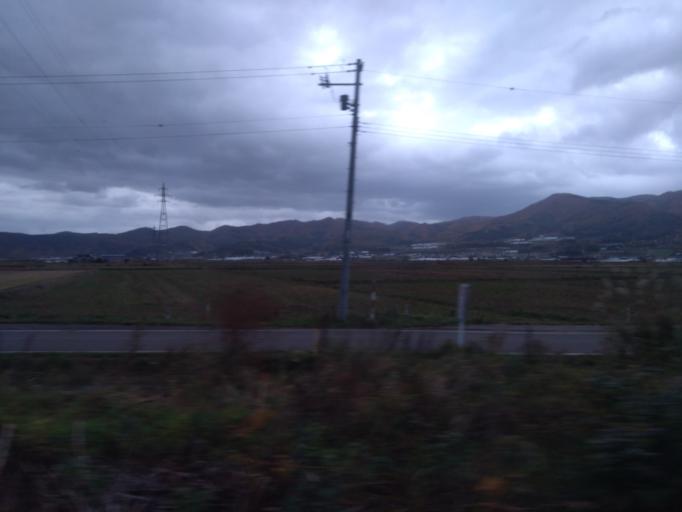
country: JP
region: Hokkaido
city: Nanae
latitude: 41.9016
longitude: 140.6661
